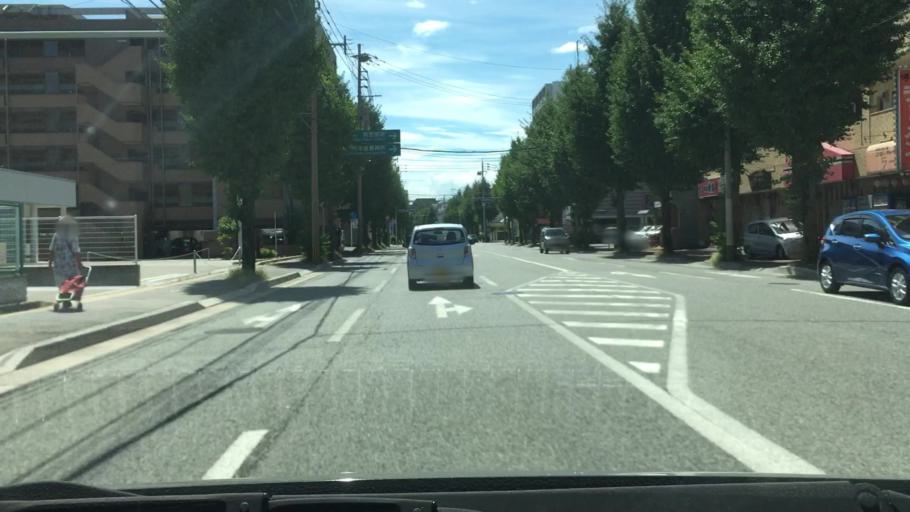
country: JP
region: Fukuoka
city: Fukuoka-shi
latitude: 33.5672
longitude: 130.4270
